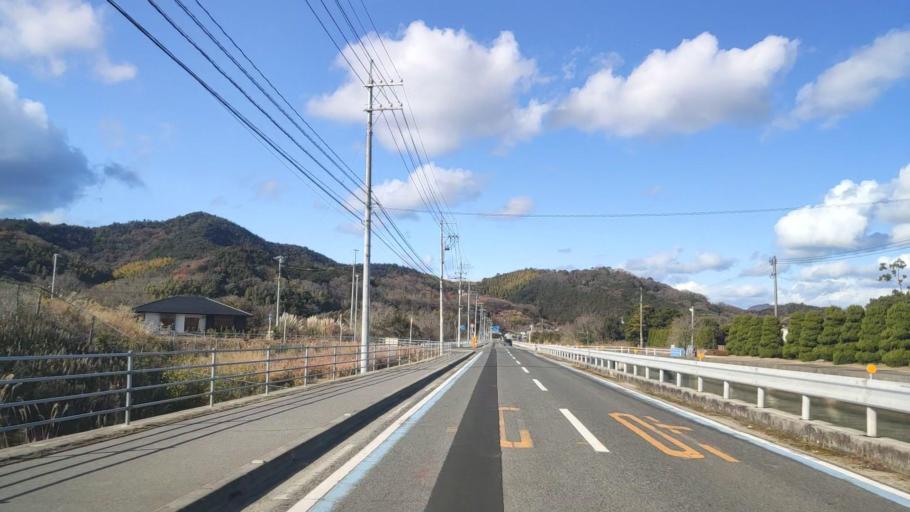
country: JP
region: Hiroshima
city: Innoshima
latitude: 34.2145
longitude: 133.1089
